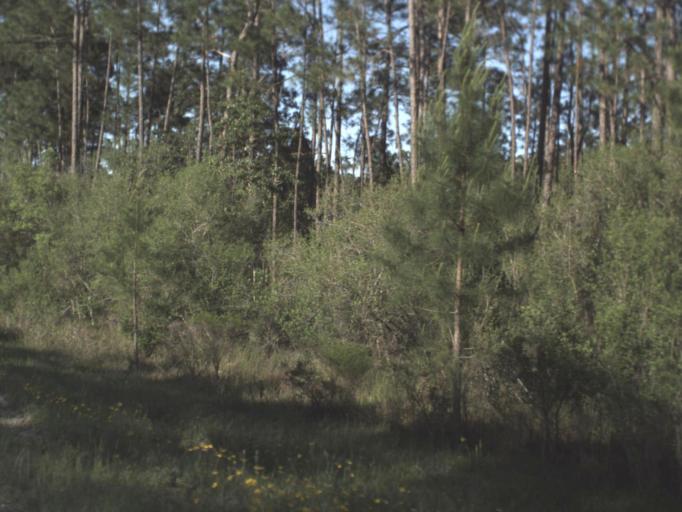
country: US
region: Florida
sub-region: Liberty County
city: Bristol
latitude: 30.2972
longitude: -84.8326
